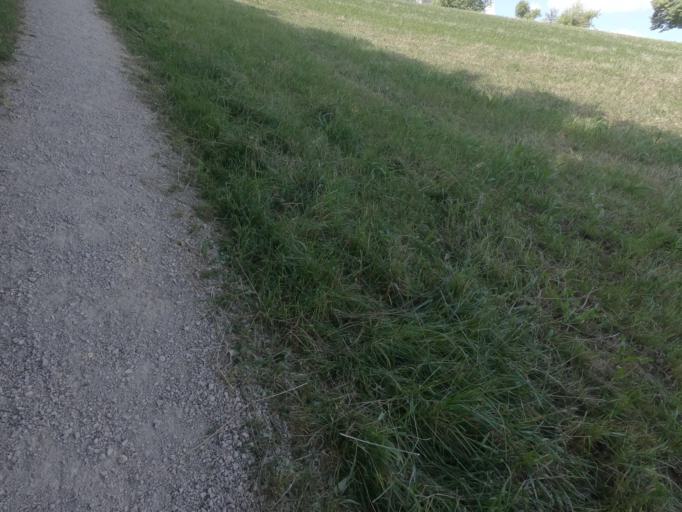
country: CH
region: Solothurn
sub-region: Bezirk Lebern
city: Langendorf
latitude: 47.2369
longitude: 7.5304
